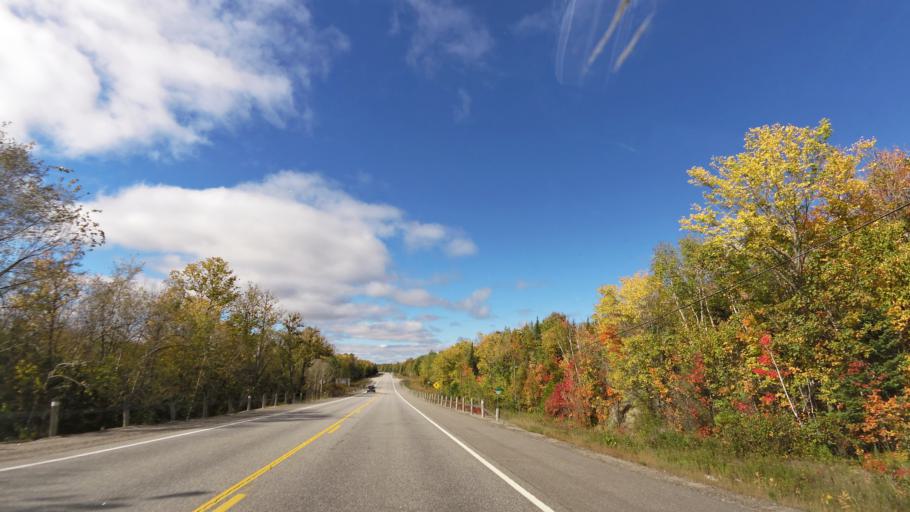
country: CA
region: Ontario
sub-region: Nipissing District
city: North Bay
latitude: 46.3672
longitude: -79.6887
